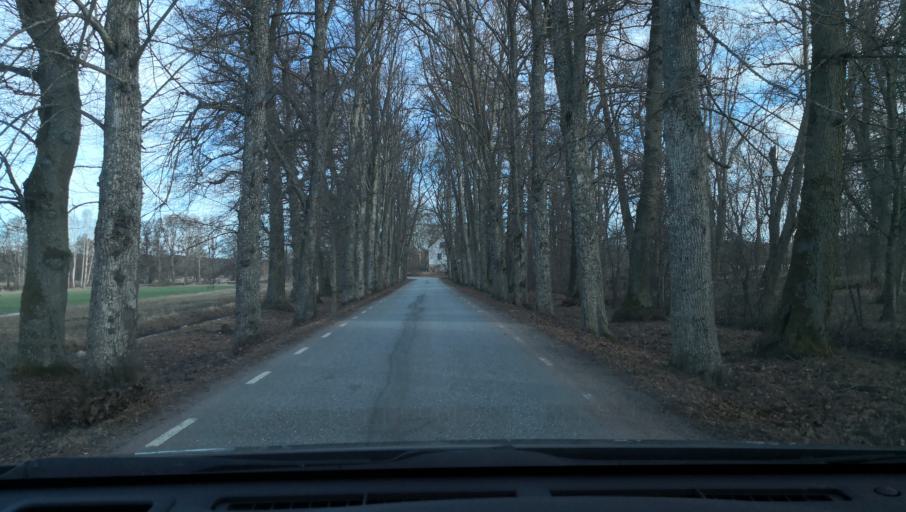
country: SE
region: Uppsala
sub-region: Enkopings Kommun
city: Grillby
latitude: 59.5424
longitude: 17.1979
